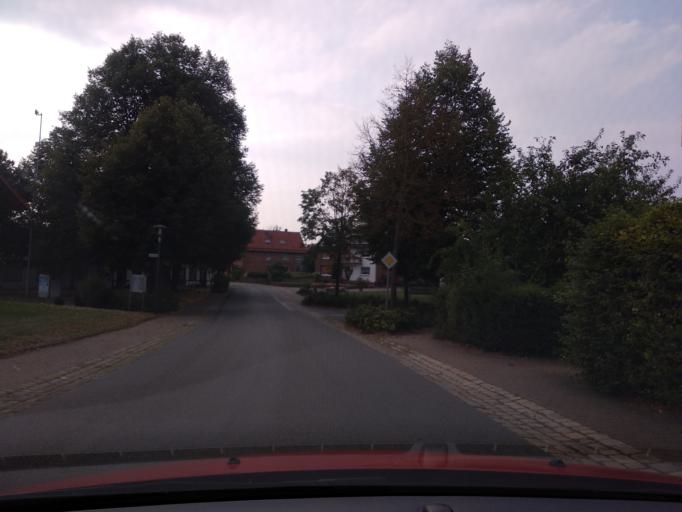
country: DE
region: Hesse
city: Liebenau
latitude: 51.5349
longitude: 9.2788
